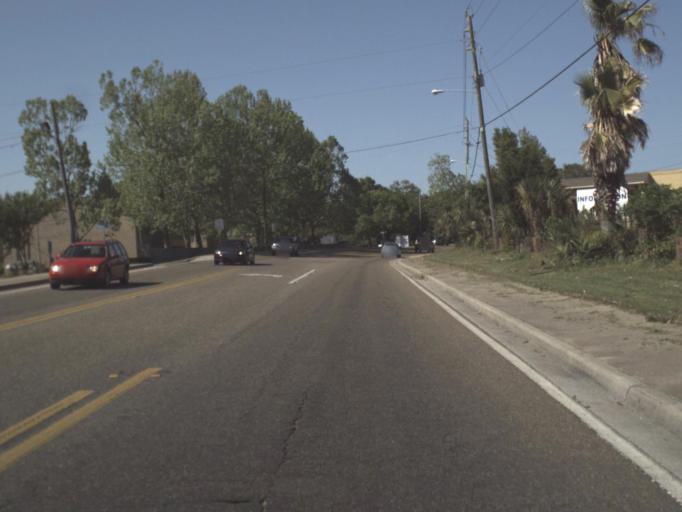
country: US
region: Florida
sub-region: Escambia County
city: East Pensacola Heights
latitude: 30.4321
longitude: -87.1755
